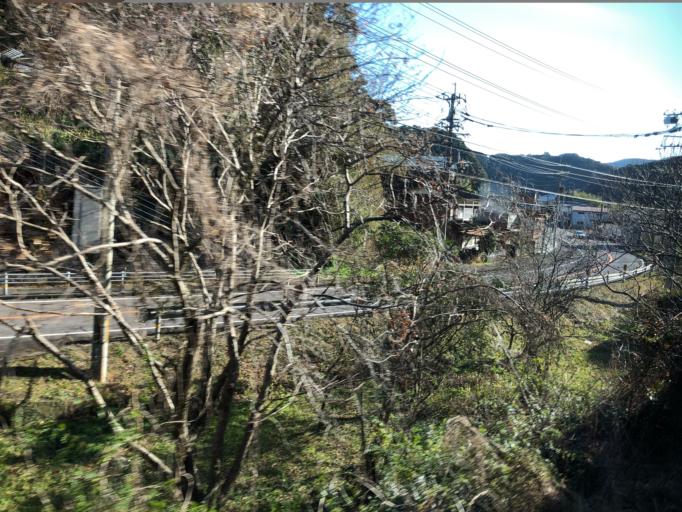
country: JP
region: Kochi
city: Nakamura
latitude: 33.1084
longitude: 133.0992
